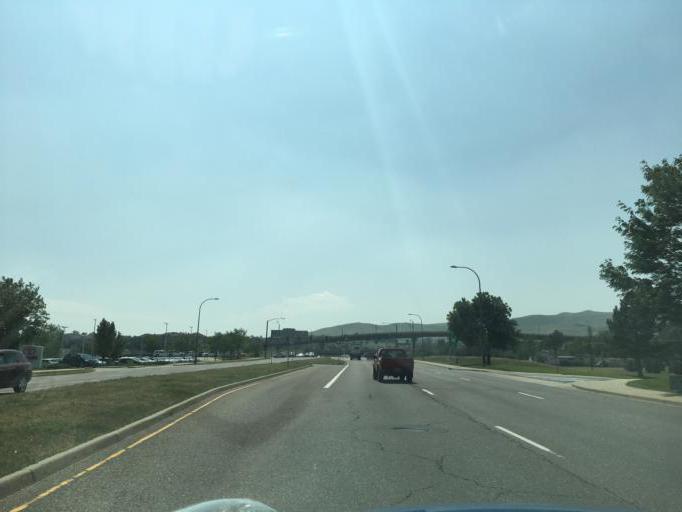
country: US
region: Colorado
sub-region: Jefferson County
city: West Pleasant View
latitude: 39.7293
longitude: -105.1655
